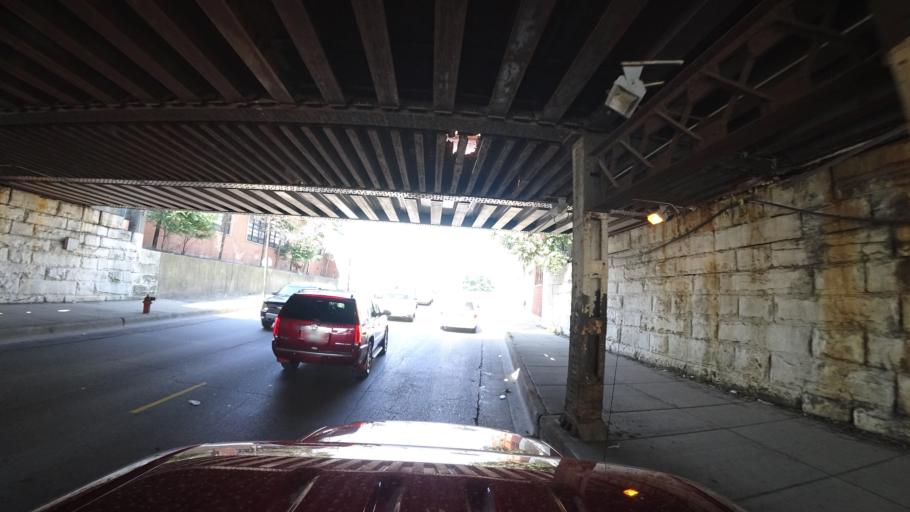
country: US
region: Illinois
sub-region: Cook County
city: Chicago
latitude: 41.8092
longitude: -87.6288
